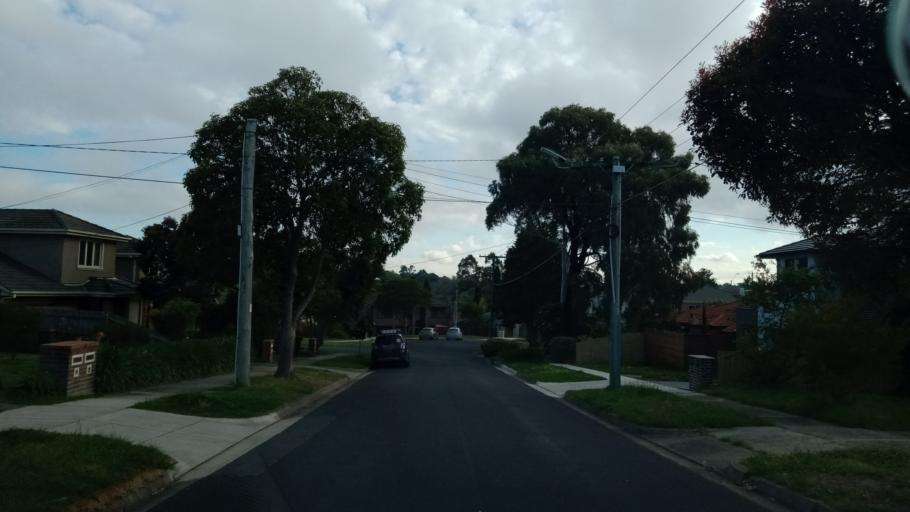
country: AU
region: Victoria
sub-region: Monash
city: Notting Hill
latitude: -37.8882
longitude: 145.1442
